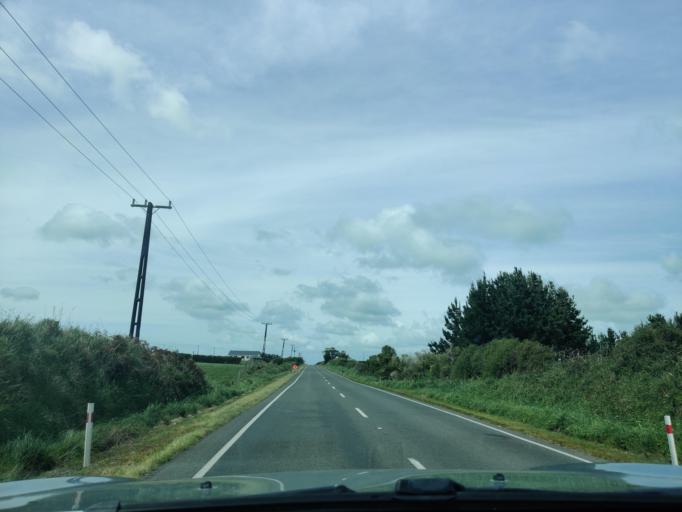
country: NZ
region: Taranaki
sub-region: South Taranaki District
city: Eltham
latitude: -39.4280
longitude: 174.1634
